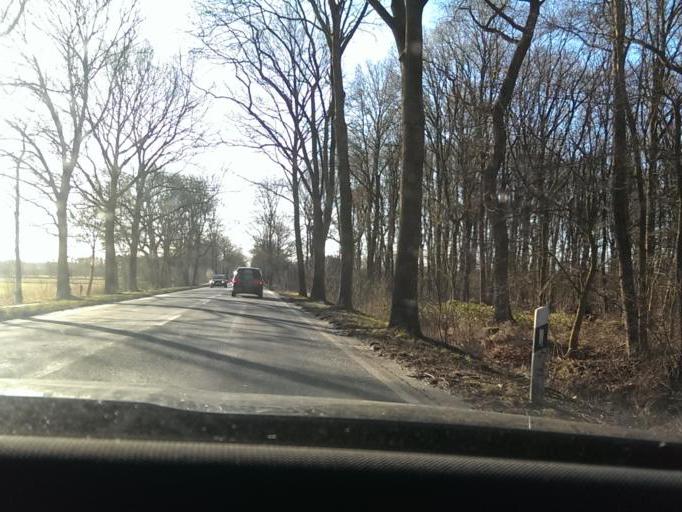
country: DE
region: Lower Saxony
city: Langenhagen
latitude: 52.5030
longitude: 9.7277
